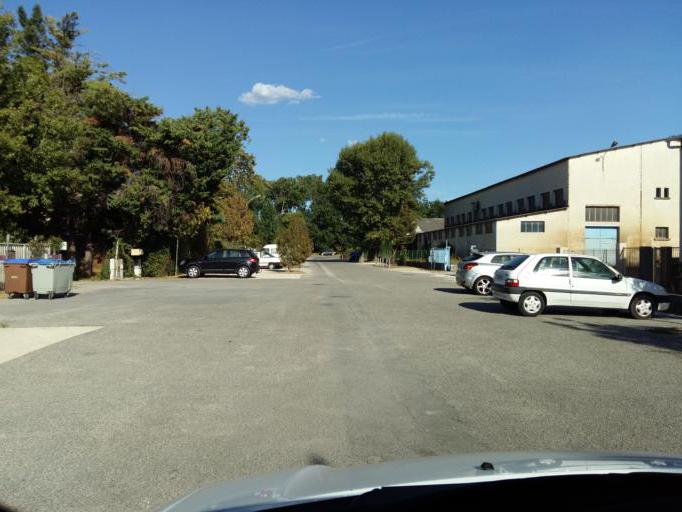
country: FR
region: Provence-Alpes-Cote d'Azur
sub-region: Departement du Vaucluse
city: L'Isle-sur-la-Sorgue
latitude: 43.9207
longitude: 5.0326
